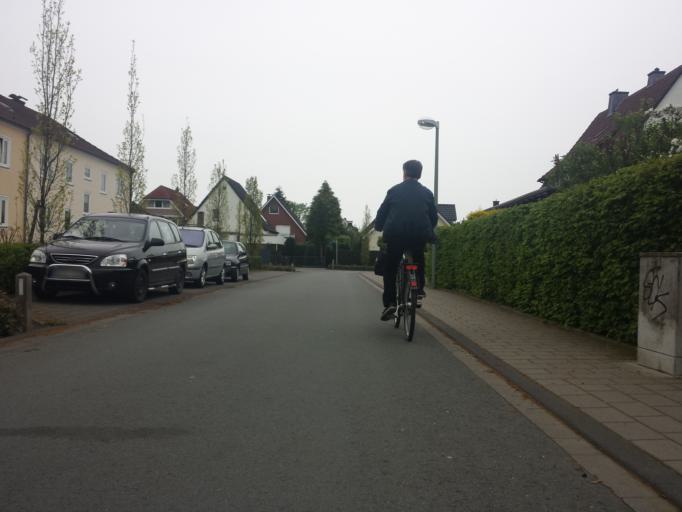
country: DE
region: North Rhine-Westphalia
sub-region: Regierungsbezirk Detmold
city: Guetersloh
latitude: 51.8908
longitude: 8.3774
